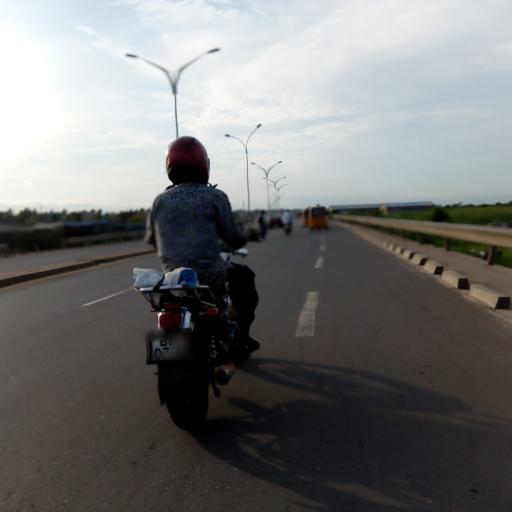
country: TG
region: Maritime
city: Lome
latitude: 6.1864
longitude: 1.2777
